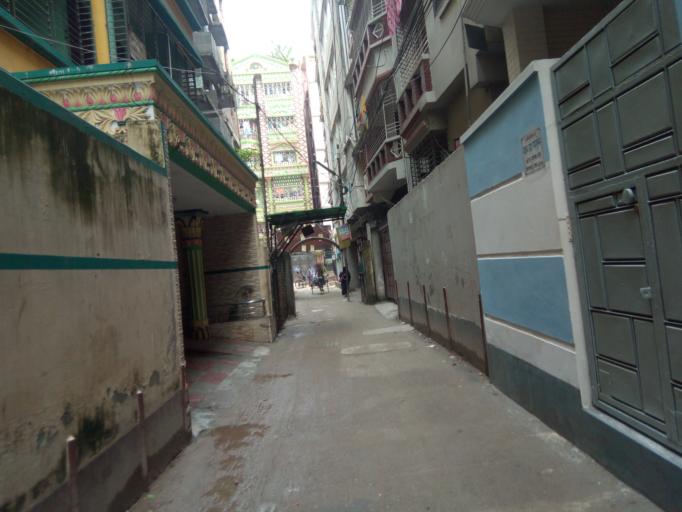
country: BD
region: Dhaka
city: Azimpur
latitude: 23.7398
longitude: 90.3681
